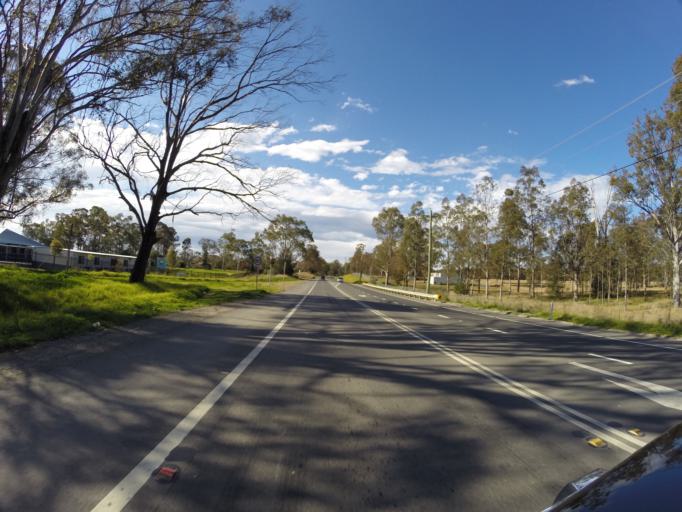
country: AU
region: New South Wales
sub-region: Fairfield
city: Cecil Park
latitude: -33.8773
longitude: 150.8261
